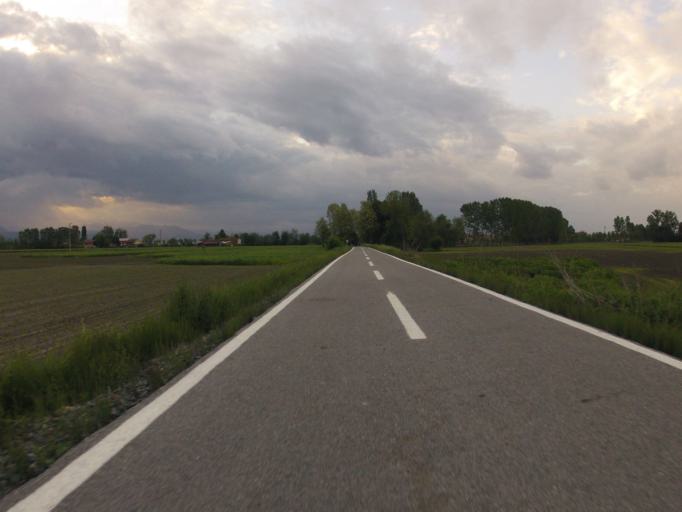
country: IT
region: Piedmont
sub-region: Provincia di Torino
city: Vigone
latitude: 44.8297
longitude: 7.4935
